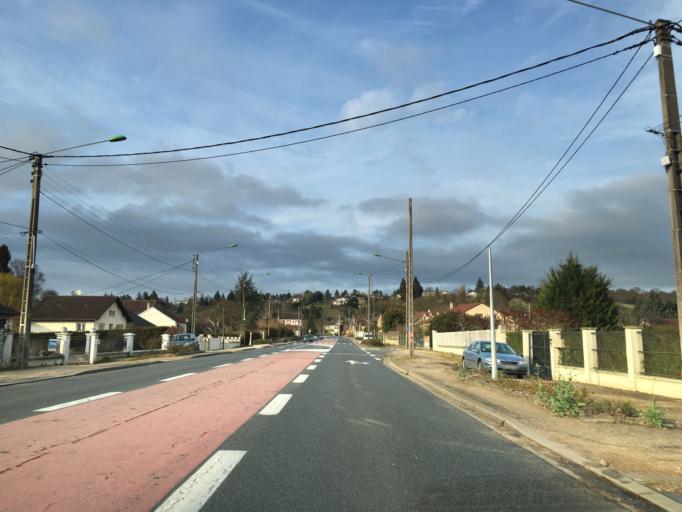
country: FR
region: Bourgogne
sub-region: Departement de l'Yonne
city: Veron
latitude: 48.1484
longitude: 3.3081
